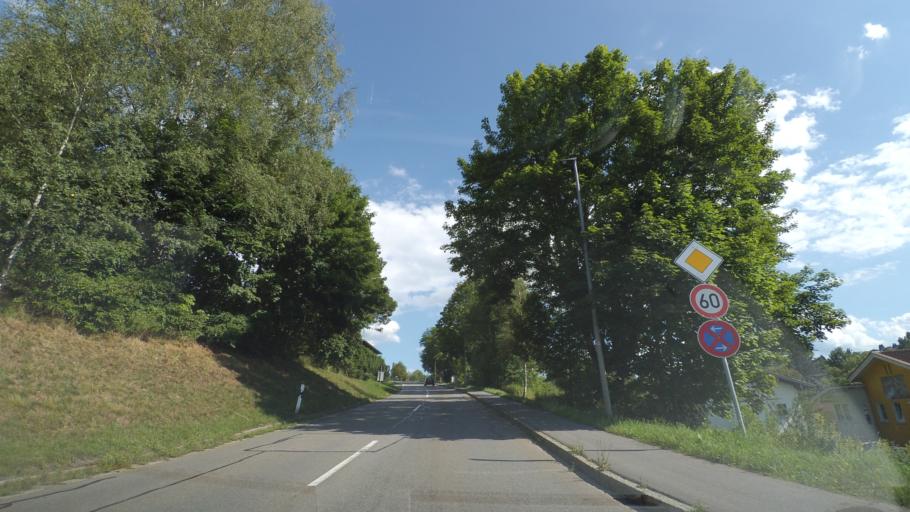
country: DE
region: Bavaria
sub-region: Lower Bavaria
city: Viechtach
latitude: 49.0810
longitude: 12.8922
